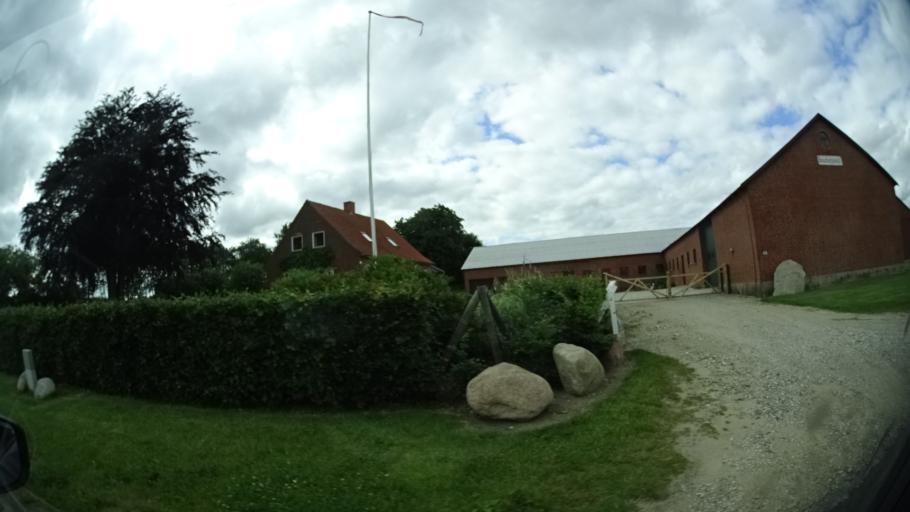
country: DK
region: Central Jutland
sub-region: Syddjurs Kommune
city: Ryomgard
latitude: 56.4130
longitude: 10.5814
